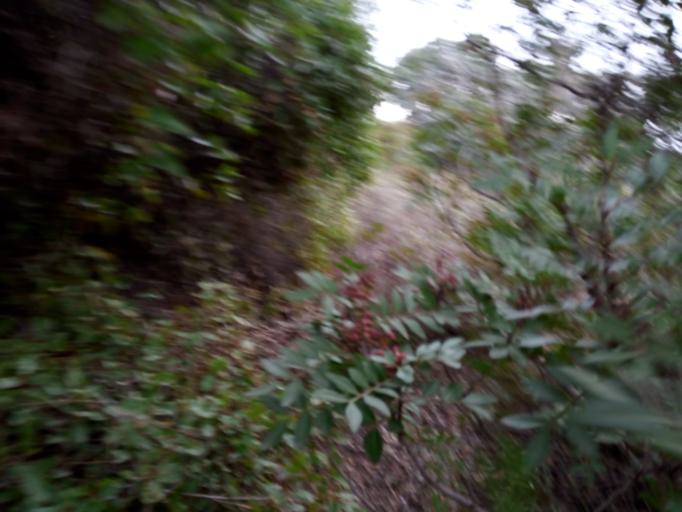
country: PT
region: Faro
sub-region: Faro
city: Santa Barbara de Nexe
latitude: 37.1029
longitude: -7.9598
